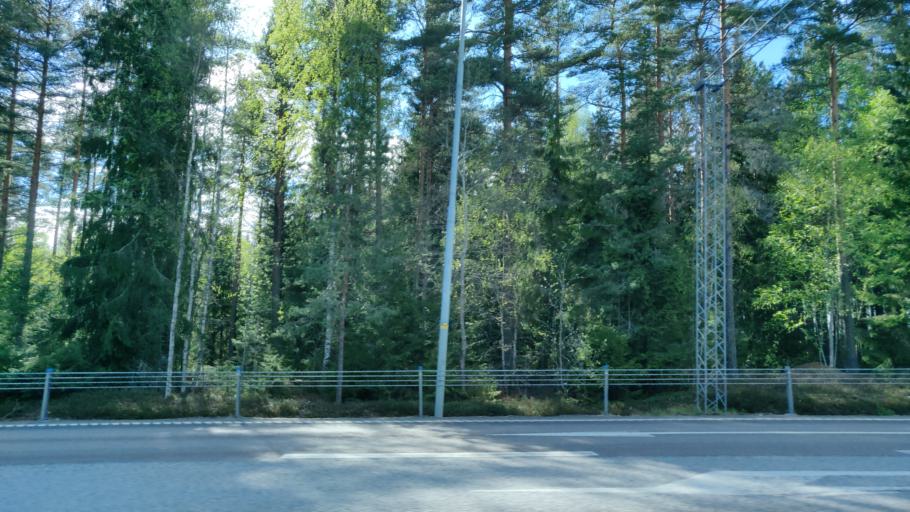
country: SE
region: Vaermland
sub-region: Forshaga Kommun
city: Forshaga
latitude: 59.4559
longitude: 13.4166
